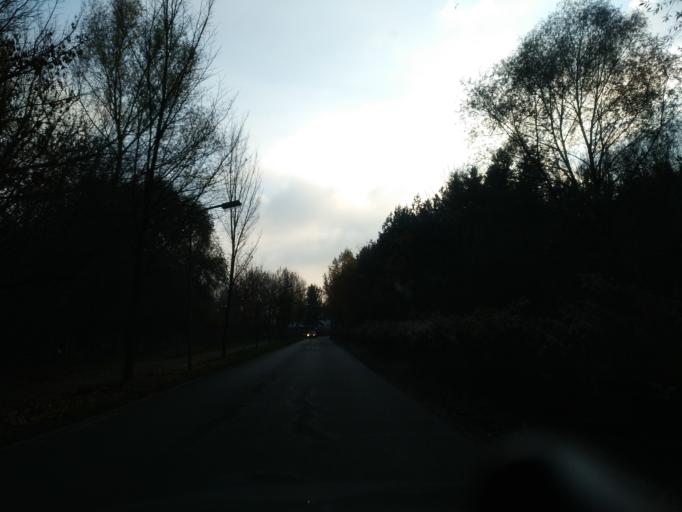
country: DE
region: Berlin
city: Falkenhagener Feld
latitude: 52.5605
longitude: 13.1456
